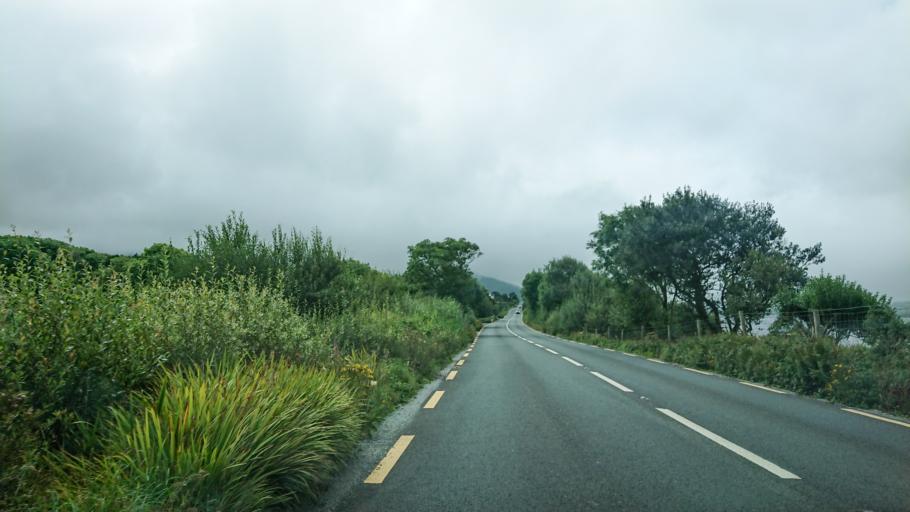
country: IE
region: Munster
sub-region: Ciarrai
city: Cahersiveen
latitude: 51.9607
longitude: -10.1840
